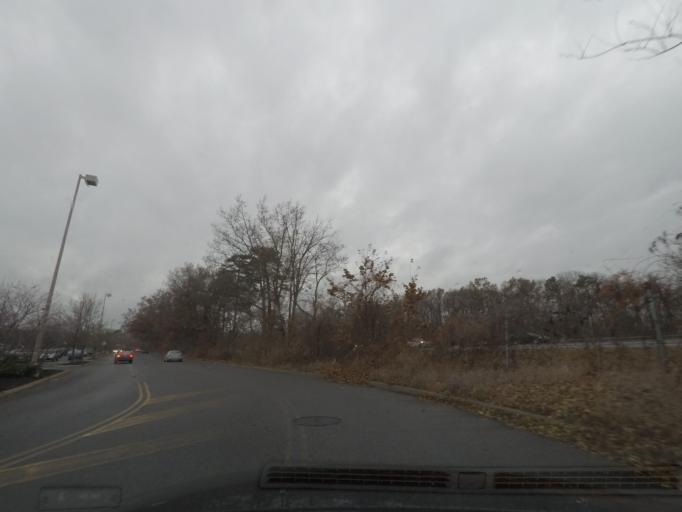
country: US
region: New York
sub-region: Albany County
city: Colonie
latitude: 42.7074
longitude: -73.8290
